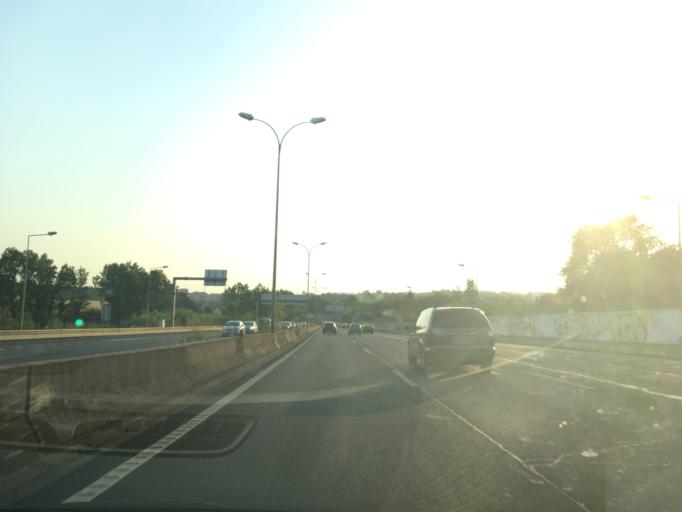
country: PT
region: Lisbon
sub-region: Sintra
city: Queluz
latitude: 38.7493
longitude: -9.2494
